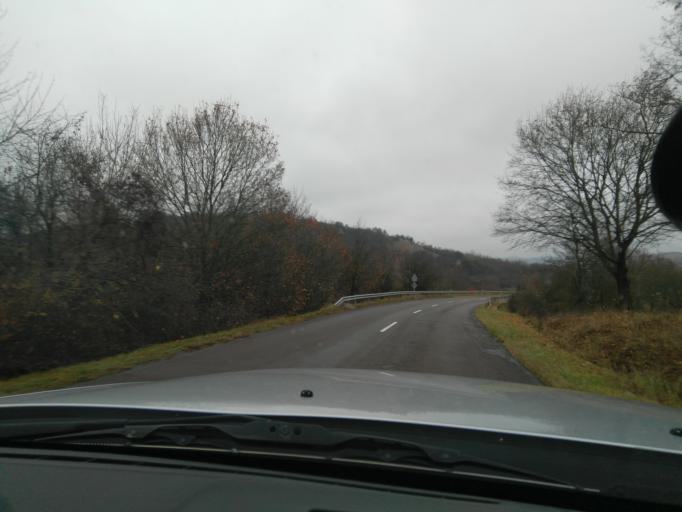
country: HU
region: Nograd
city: Matraterenye
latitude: 48.0466
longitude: 19.9136
